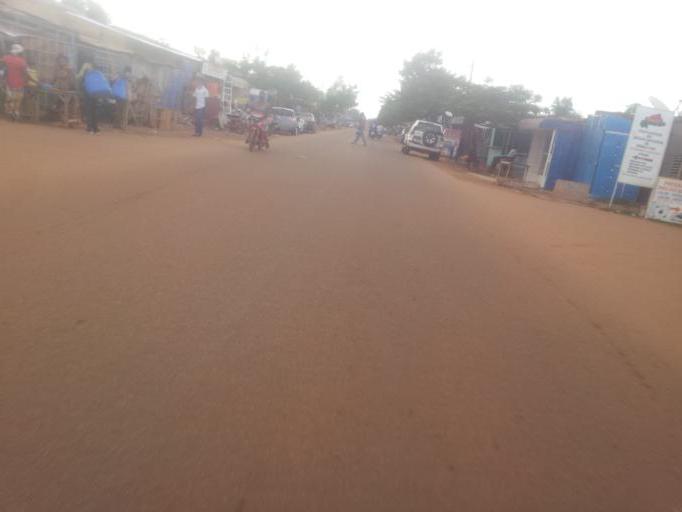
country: BF
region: Centre
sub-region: Kadiogo Province
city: Ouagadougou
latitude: 12.3801
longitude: -1.5399
